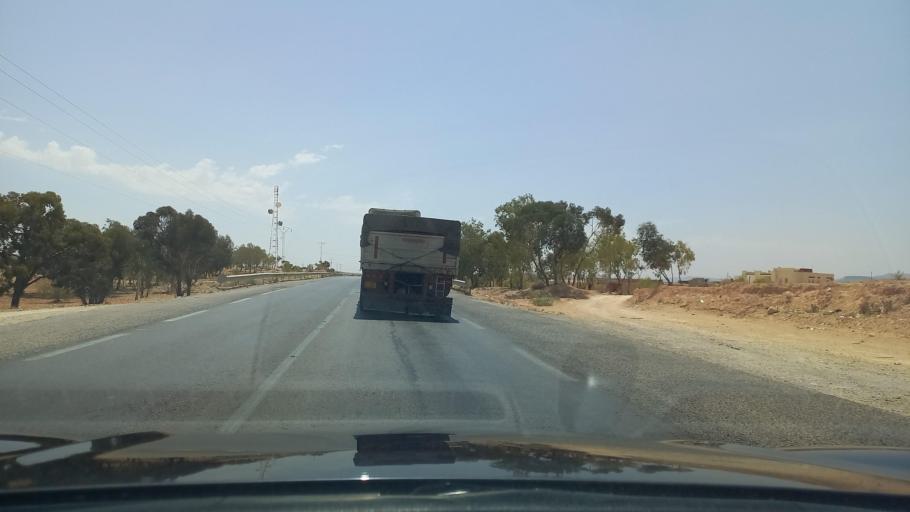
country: TN
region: Madanin
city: Medenine
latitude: 33.5718
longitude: 10.3171
